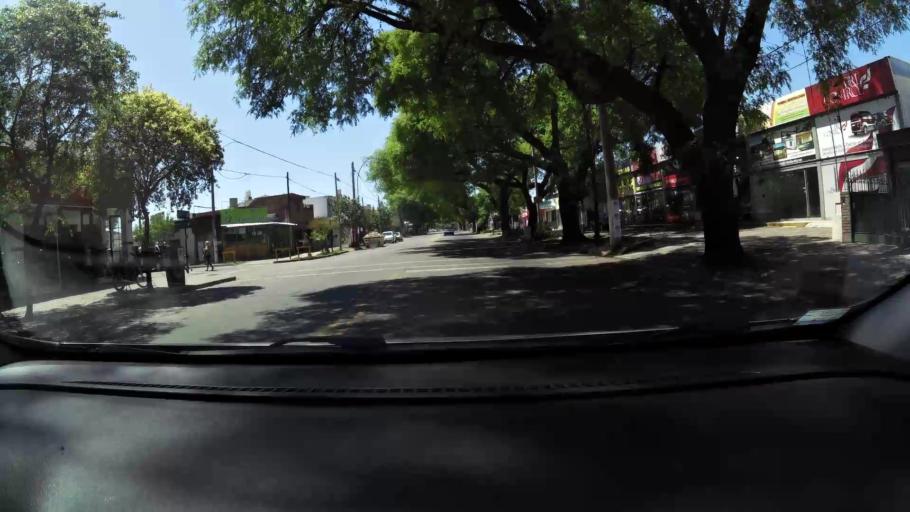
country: AR
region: Cordoba
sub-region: Departamento de Capital
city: Cordoba
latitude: -31.3785
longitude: -64.2071
